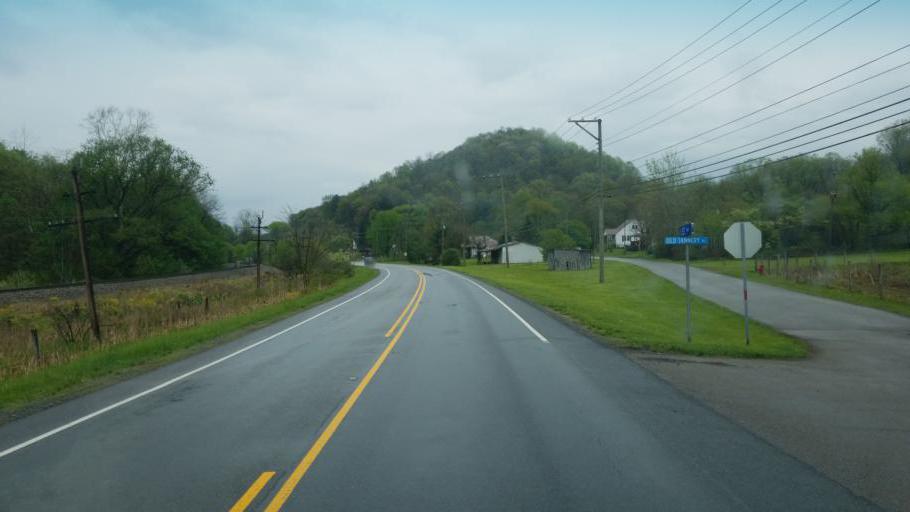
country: US
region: Virginia
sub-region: Smyth County
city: Atkins
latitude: 36.8778
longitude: -81.3855
